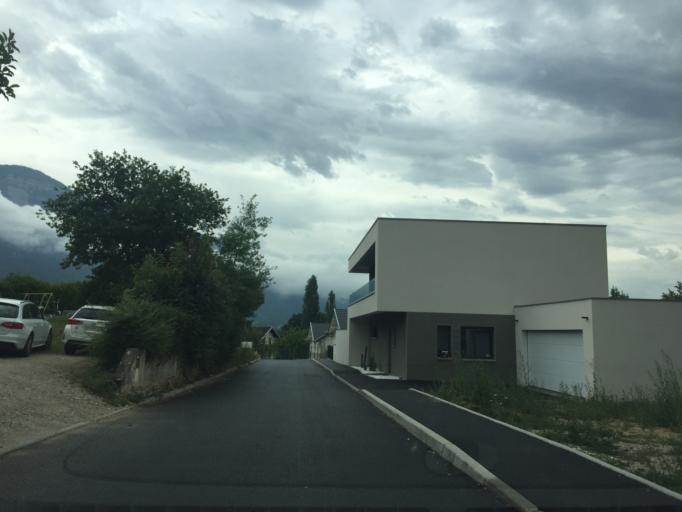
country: FR
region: Rhone-Alpes
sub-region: Departement de la Savoie
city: Aix-les-Bains
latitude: 45.6739
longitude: 5.9196
